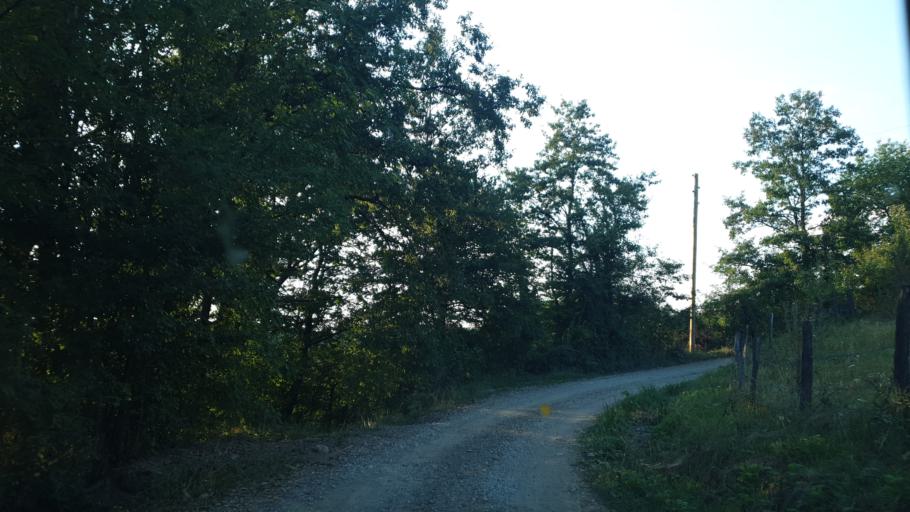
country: RS
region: Central Serbia
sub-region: Zlatiborski Okrug
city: Kosjeric
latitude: 43.9973
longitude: 20.0032
